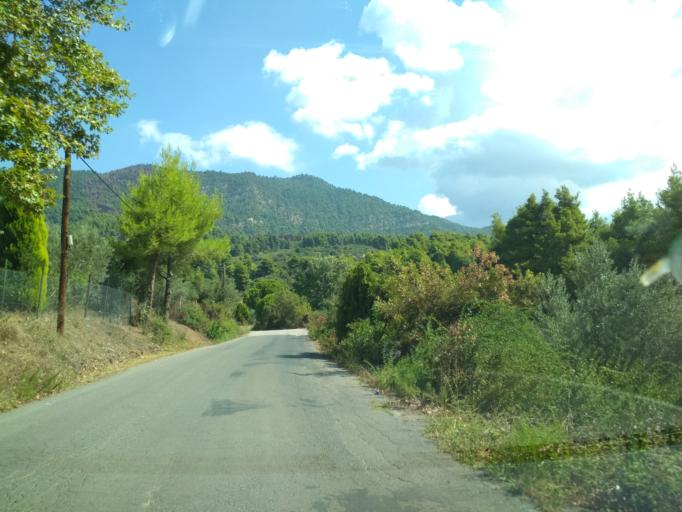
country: GR
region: Central Greece
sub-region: Nomos Evvoias
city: Roviai
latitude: 38.8239
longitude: 23.2428
